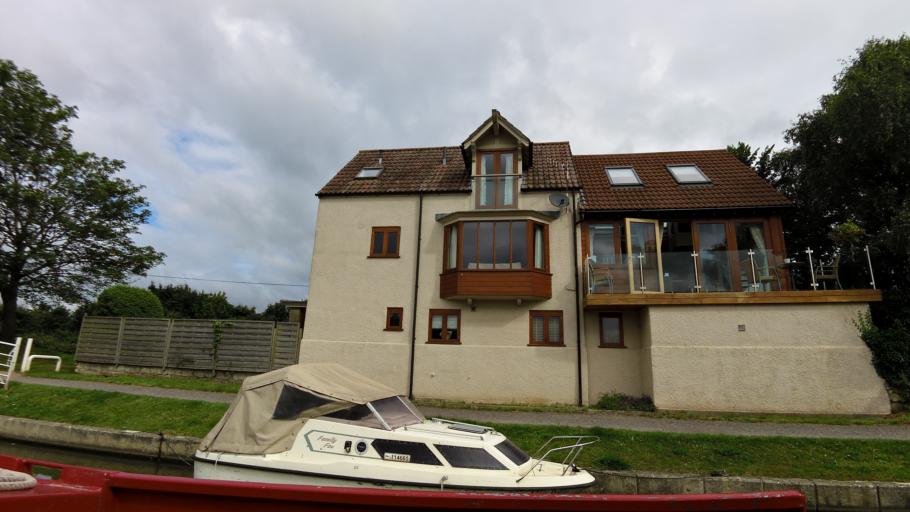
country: GB
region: England
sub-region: Bath and North East Somerset
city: Bath
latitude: 51.3974
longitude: -2.3187
